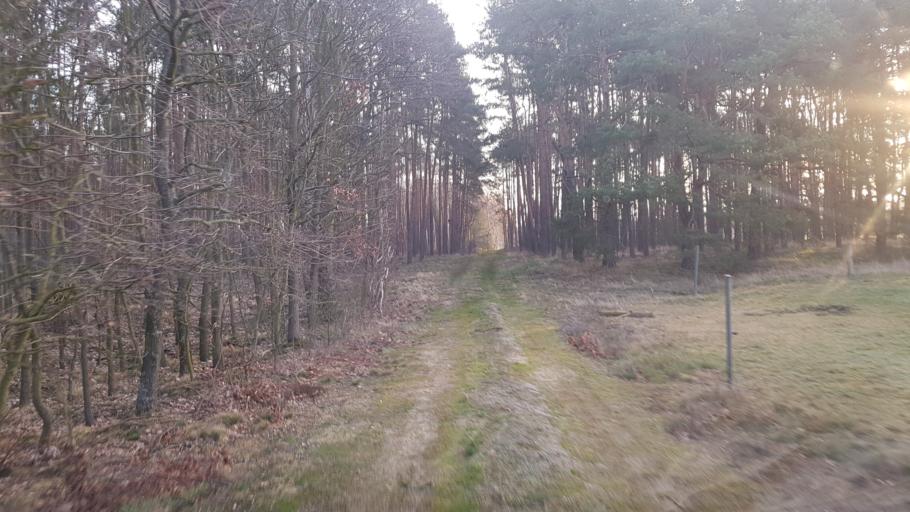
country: DE
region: Brandenburg
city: Schilda
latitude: 51.5711
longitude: 13.3250
